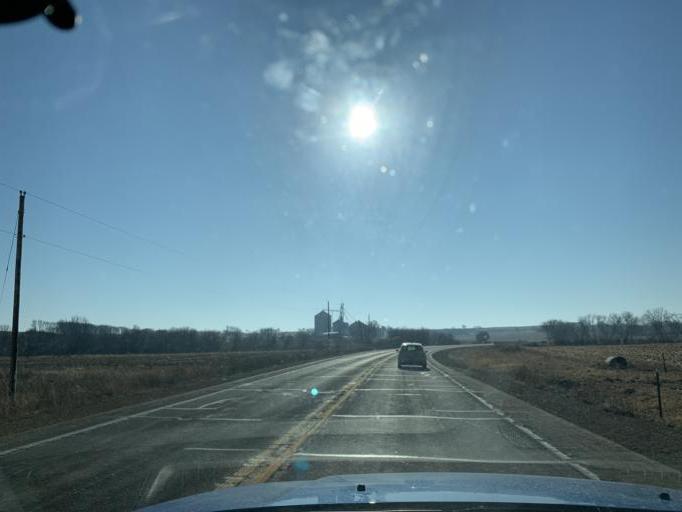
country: US
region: Wisconsin
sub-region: Green County
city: Monticello
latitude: 42.7172
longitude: -89.5983
